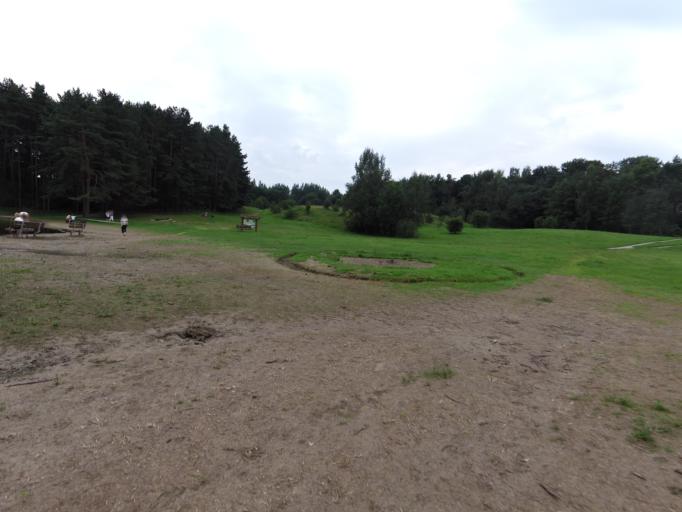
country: LT
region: Vilnius County
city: Seskine
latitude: 54.7203
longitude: 25.2631
